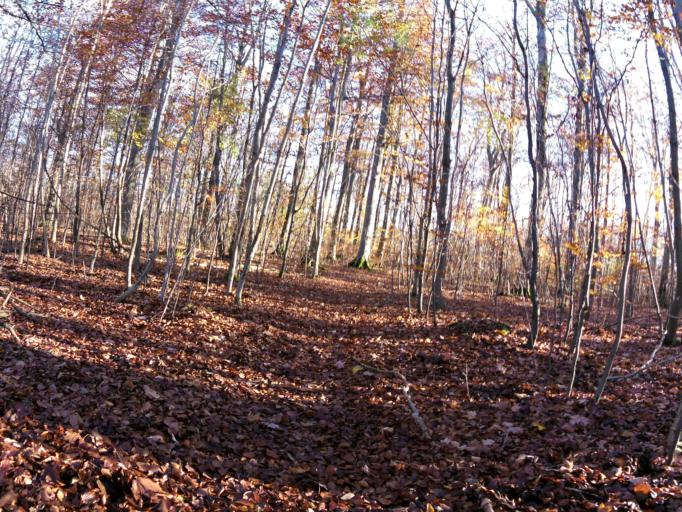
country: DE
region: Thuringia
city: Kammerforst
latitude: 51.0603
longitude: 10.4455
